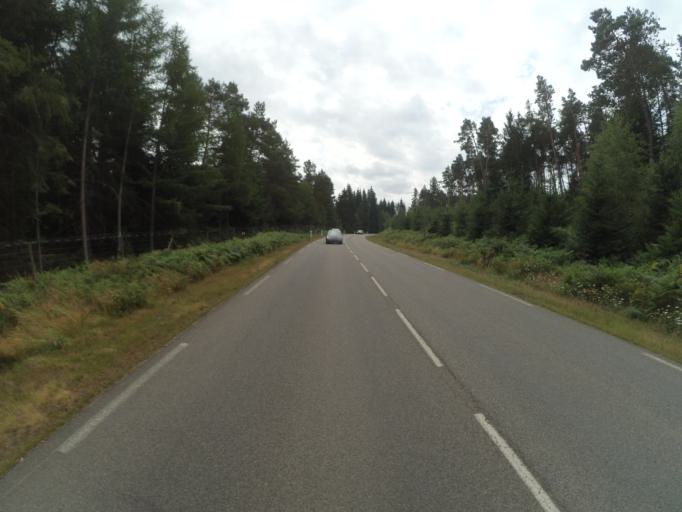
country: FR
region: Limousin
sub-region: Departement de la Correze
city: Ussel
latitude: 45.6213
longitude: 2.2878
